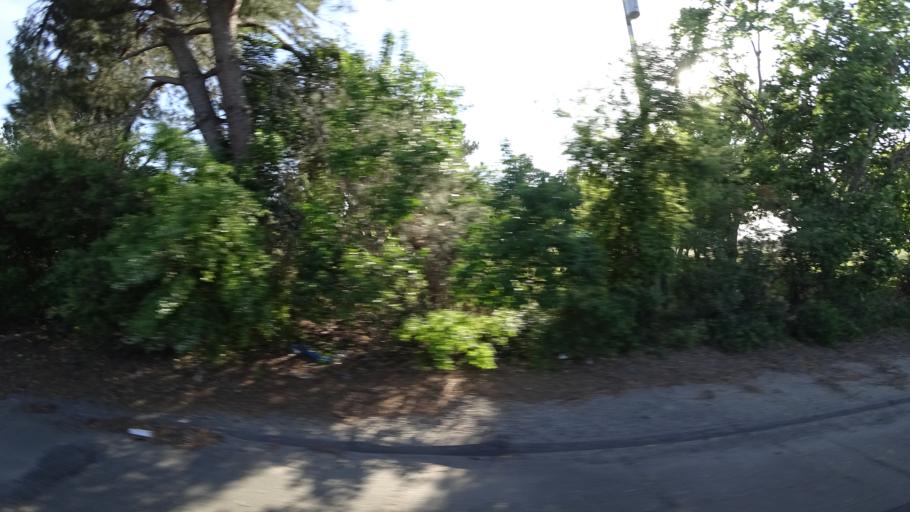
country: US
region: California
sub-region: Yuba County
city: Olivehurst
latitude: 39.0882
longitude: -121.5371
